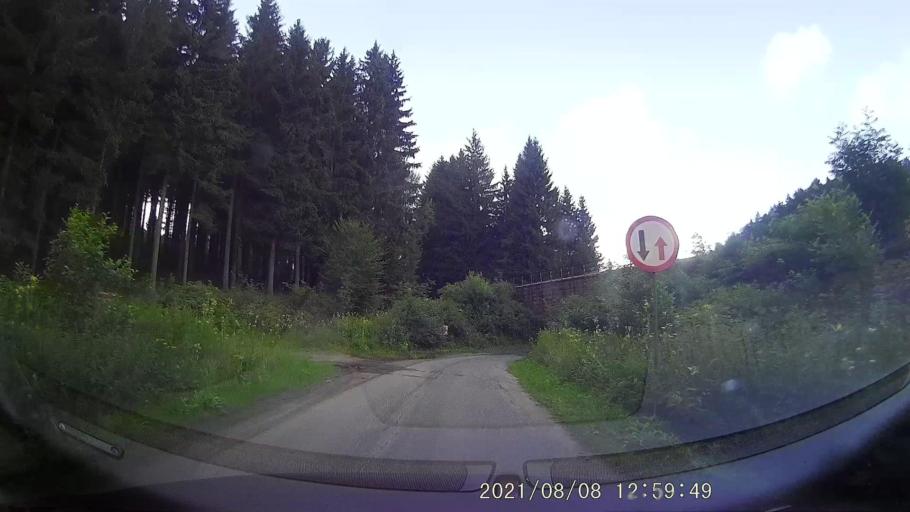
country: PL
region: Lower Silesian Voivodeship
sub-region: Powiat klodzki
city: Duszniki-Zdroj
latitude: 50.4115
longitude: 16.3462
